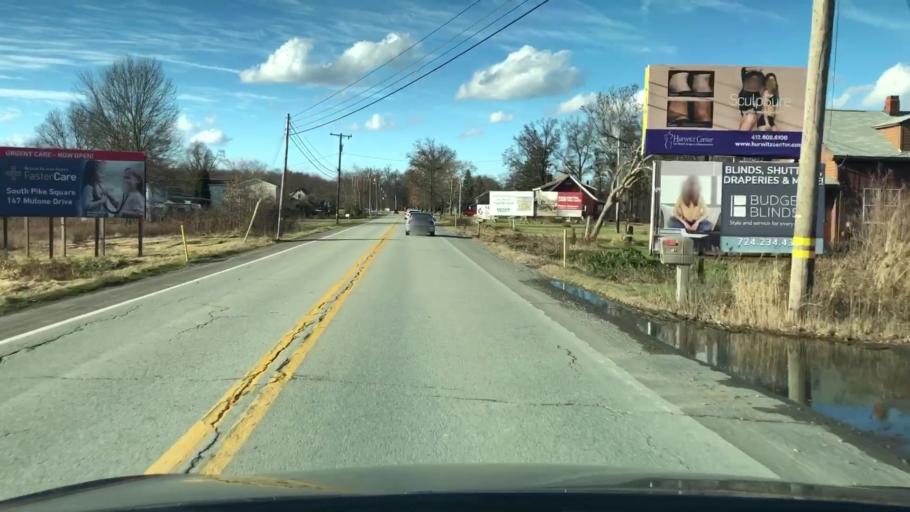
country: US
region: Pennsylvania
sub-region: Butler County
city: Saxonburg
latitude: 40.7452
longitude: -79.7678
